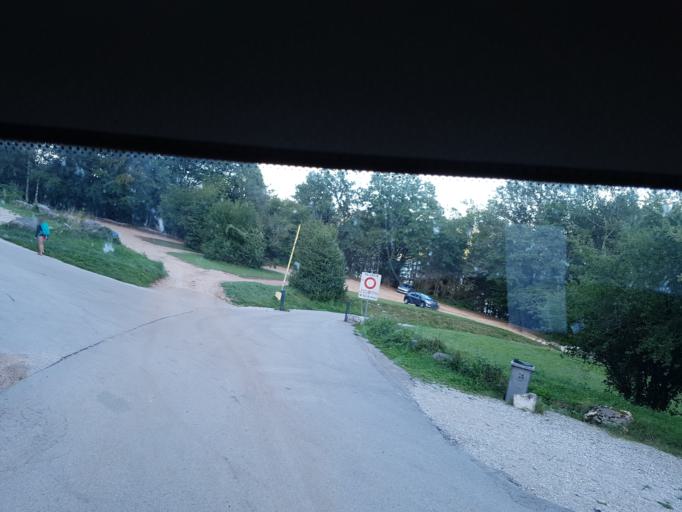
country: FR
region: Franche-Comte
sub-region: Departement du Jura
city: Orgelet
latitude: 46.4816
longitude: 5.6687
